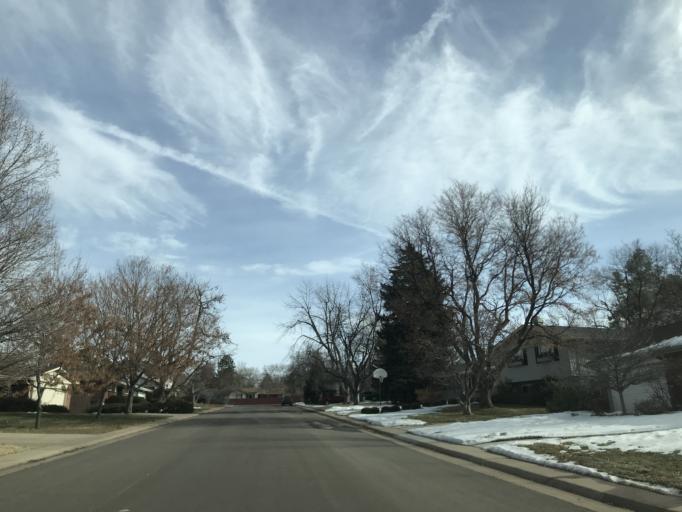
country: US
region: Colorado
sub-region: Arapahoe County
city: Columbine Valley
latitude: 39.5928
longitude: -105.0180
